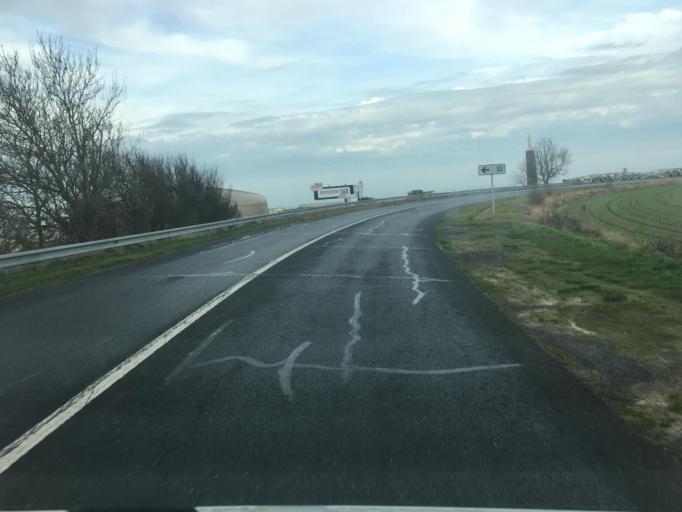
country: FR
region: Lower Normandy
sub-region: Departement du Calvados
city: Ver-sur-Mer
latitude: 49.3380
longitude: -0.6178
